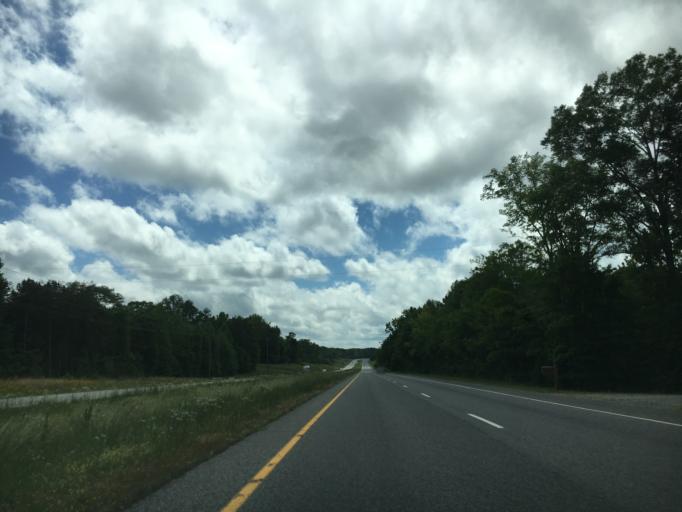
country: US
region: Virginia
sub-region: Mecklenburg County
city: Clarksville
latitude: 36.6453
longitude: -78.5060
